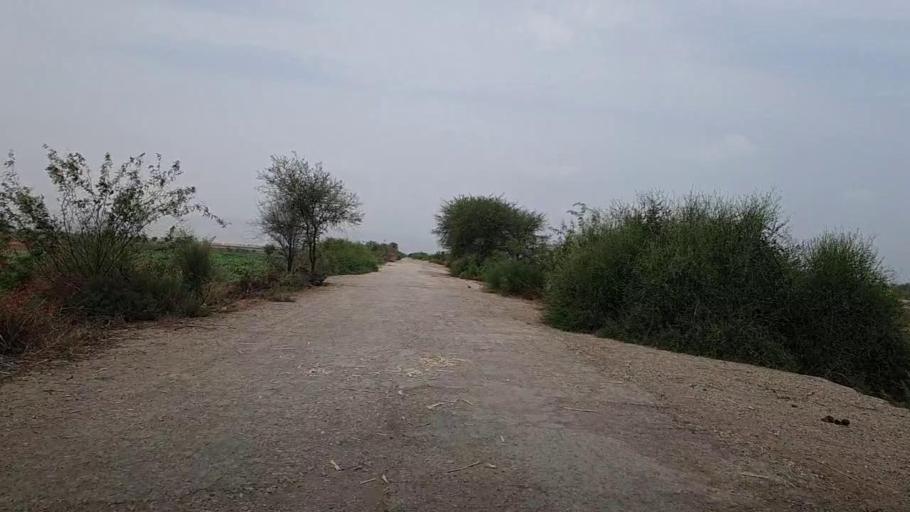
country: PK
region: Sindh
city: Sann
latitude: 26.2061
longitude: 67.9673
